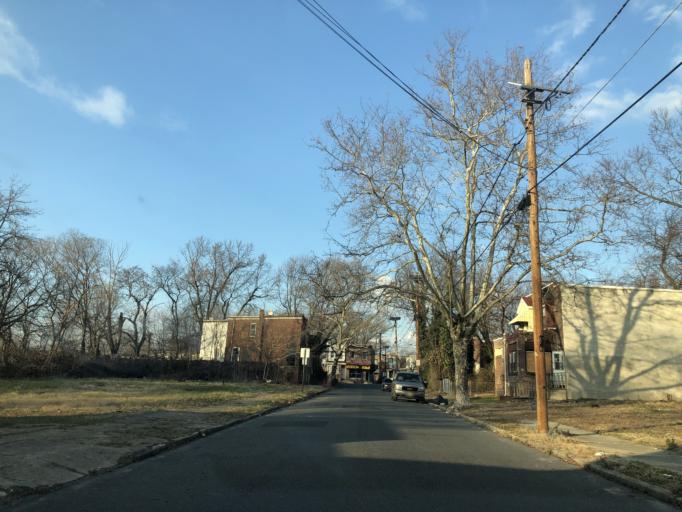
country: US
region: New Jersey
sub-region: Camden County
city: Wood-Lynne
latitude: 39.9224
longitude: -75.1071
